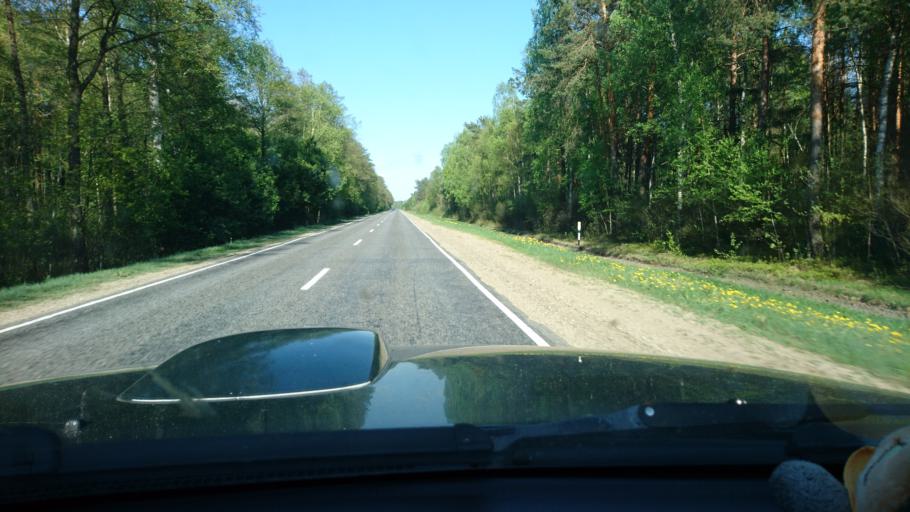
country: BY
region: Brest
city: Zhabinka
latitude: 52.3845
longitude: 24.1471
